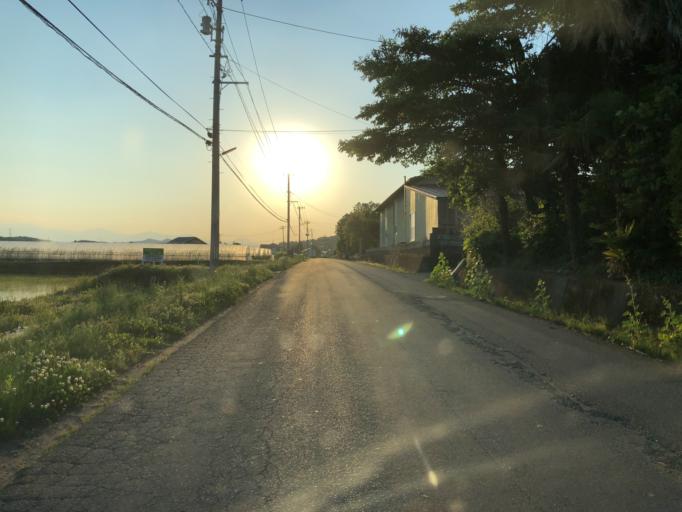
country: JP
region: Fukushima
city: Sukagawa
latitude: 37.1800
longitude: 140.3286
